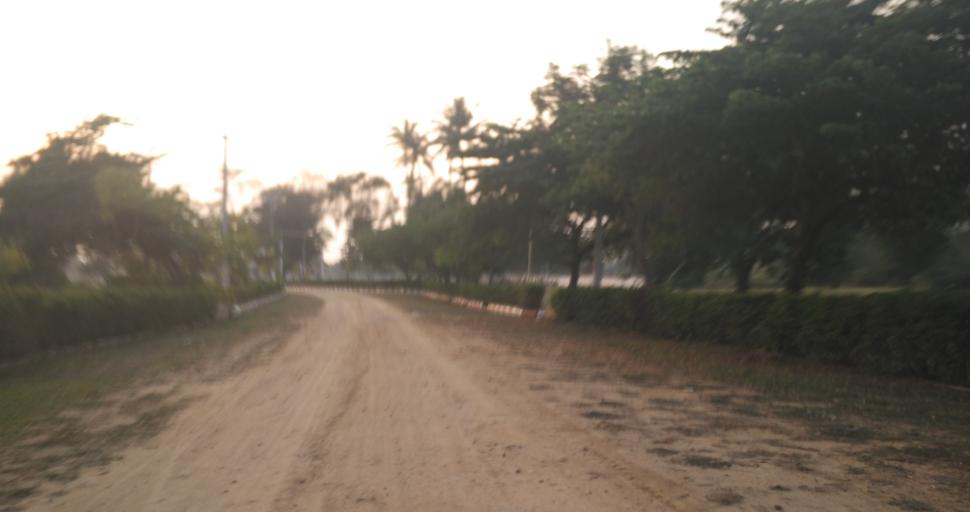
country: IN
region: Tamil Nadu
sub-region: Krishnagiri
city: Hosur
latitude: 12.6706
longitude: 77.8311
